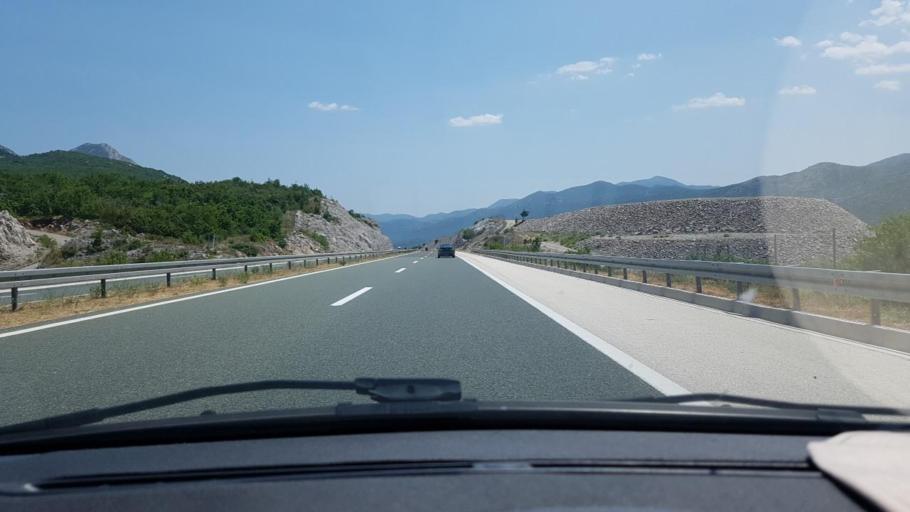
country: HR
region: Splitsko-Dalmatinska
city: Runovic
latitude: 43.3041
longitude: 17.1902
